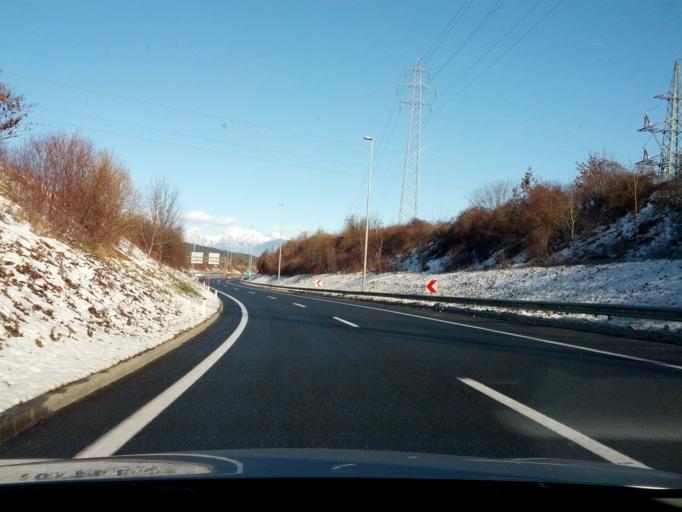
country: SI
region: Dol pri Ljubljani
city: Dol pri Ljubljani
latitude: 46.0697
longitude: 14.5784
